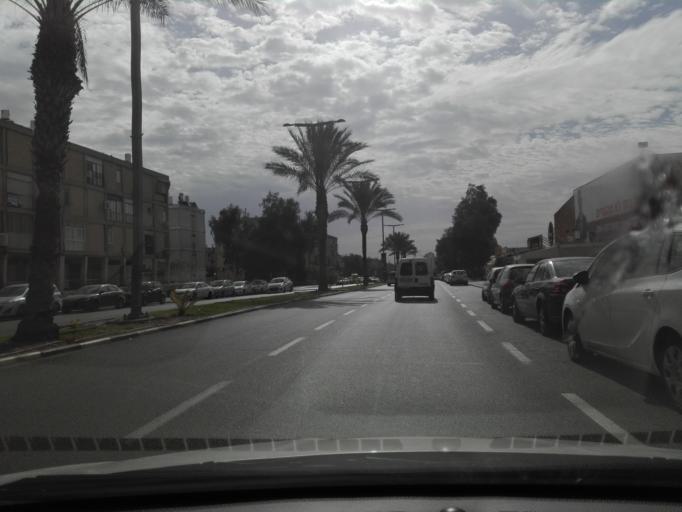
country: IL
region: Southern District
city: Beersheba
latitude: 31.2716
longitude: 34.7980
